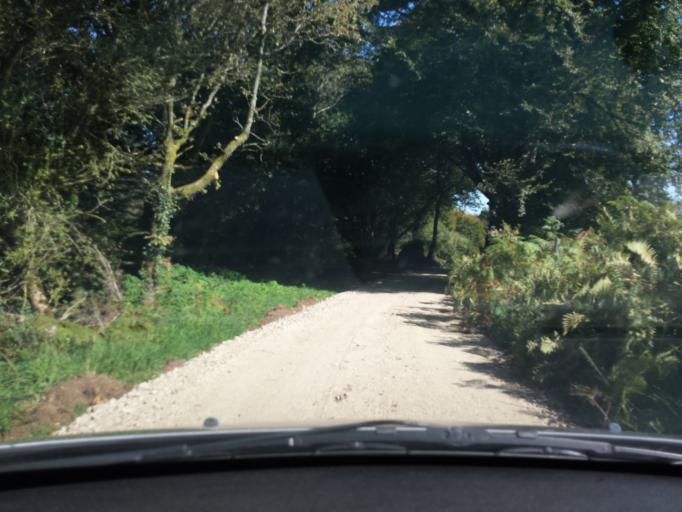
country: FR
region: Brittany
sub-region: Departement des Cotes-d'Armor
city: Plounevez-Quintin
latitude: 48.3332
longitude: -3.2551
